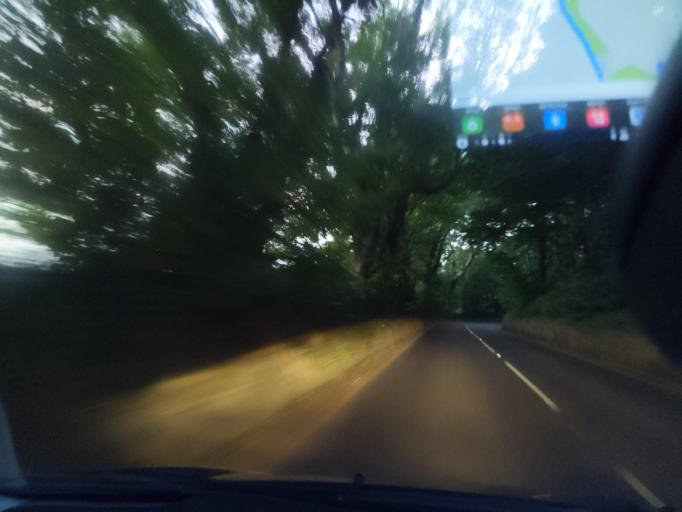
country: GB
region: England
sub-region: Cornwall
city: Camborne
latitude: 50.1957
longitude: -5.3081
